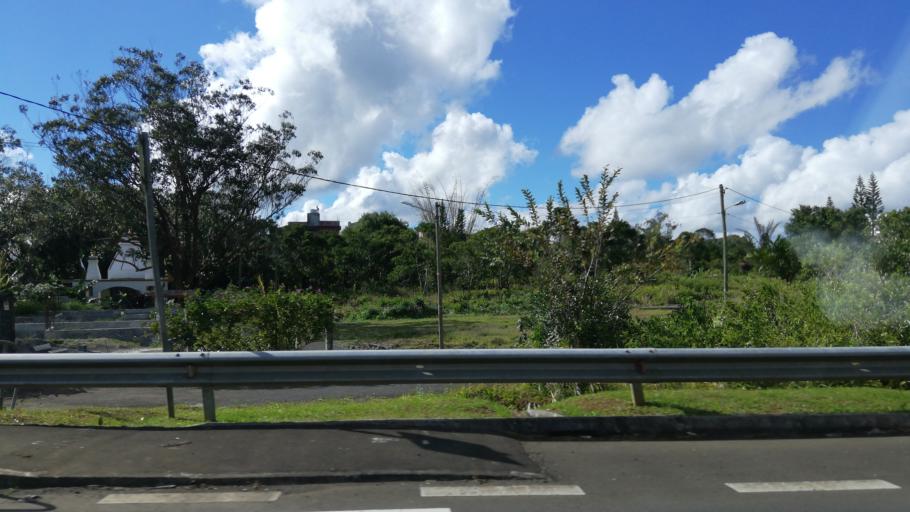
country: MU
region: Moka
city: La Dagotiere
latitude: -20.2545
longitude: 57.5638
